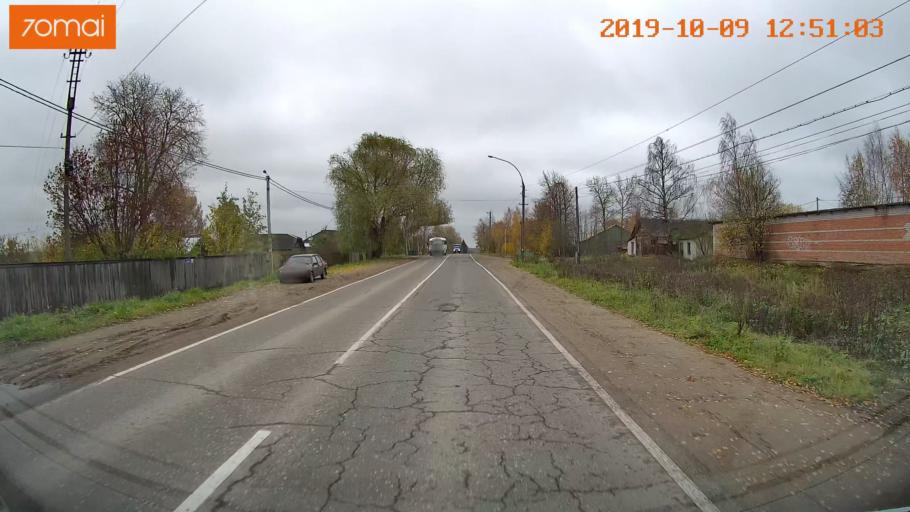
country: RU
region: Jaroslavl
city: Prechistoye
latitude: 58.4215
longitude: 40.3366
